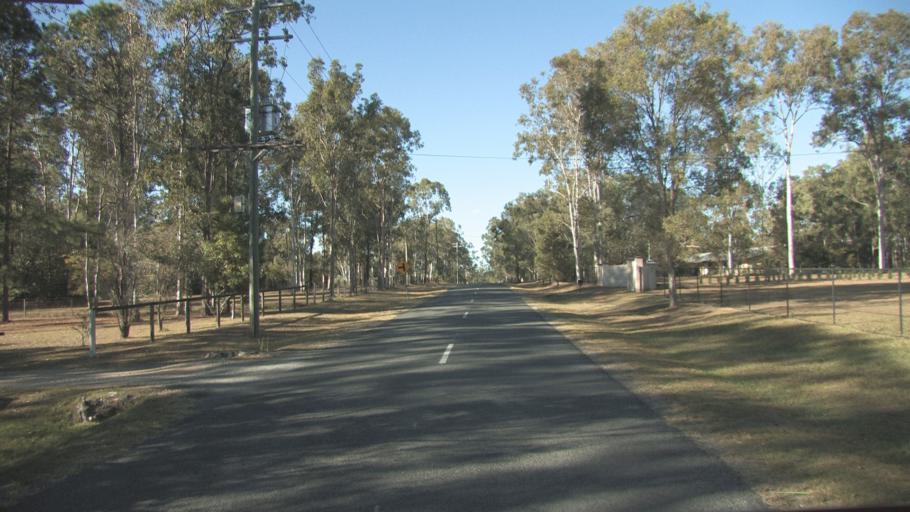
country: AU
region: Queensland
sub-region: Logan
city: North Maclean
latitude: -27.7954
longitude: 152.9885
